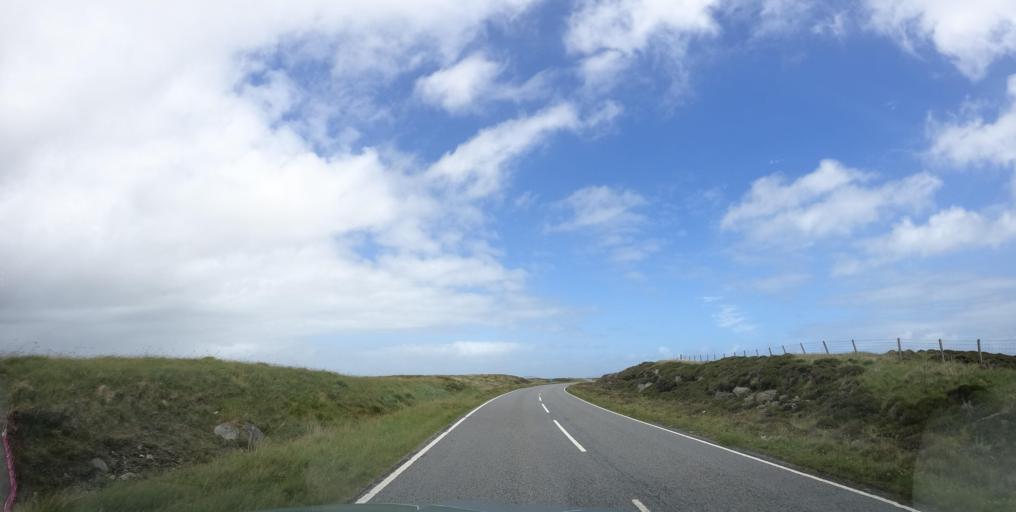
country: GB
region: Scotland
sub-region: Eilean Siar
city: Benbecula
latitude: 57.3635
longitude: -7.3544
